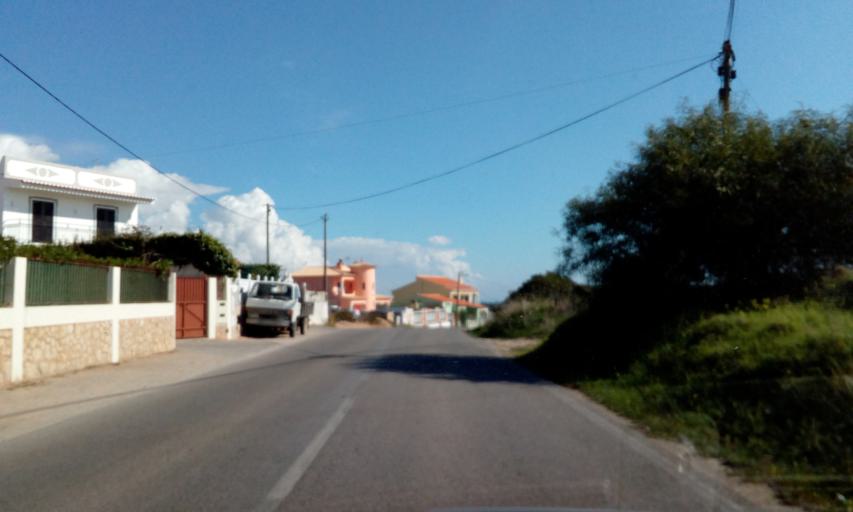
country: PT
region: Faro
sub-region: Albufeira
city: Ferreiras
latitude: 37.1175
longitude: -8.2151
